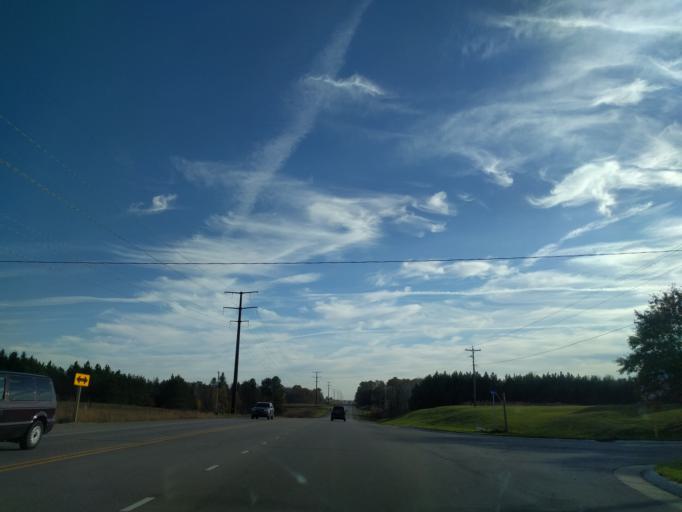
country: US
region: Wisconsin
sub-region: Marinette County
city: Peshtigo
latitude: 45.2838
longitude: -87.9909
